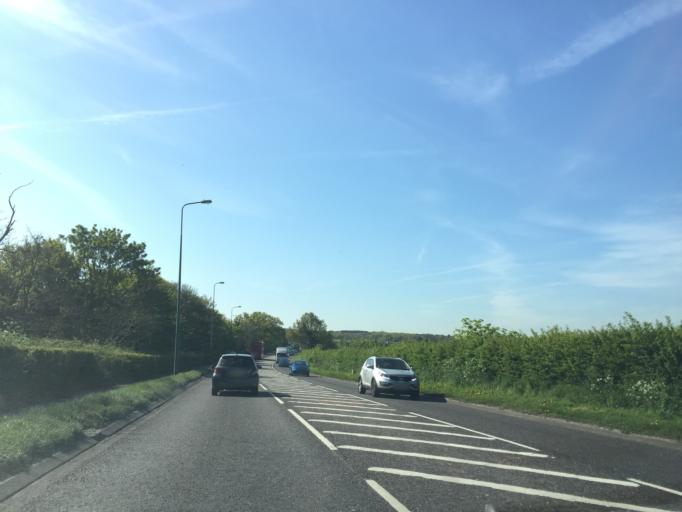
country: GB
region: England
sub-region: Essex
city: Harlow
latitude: 51.7614
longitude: 0.1266
